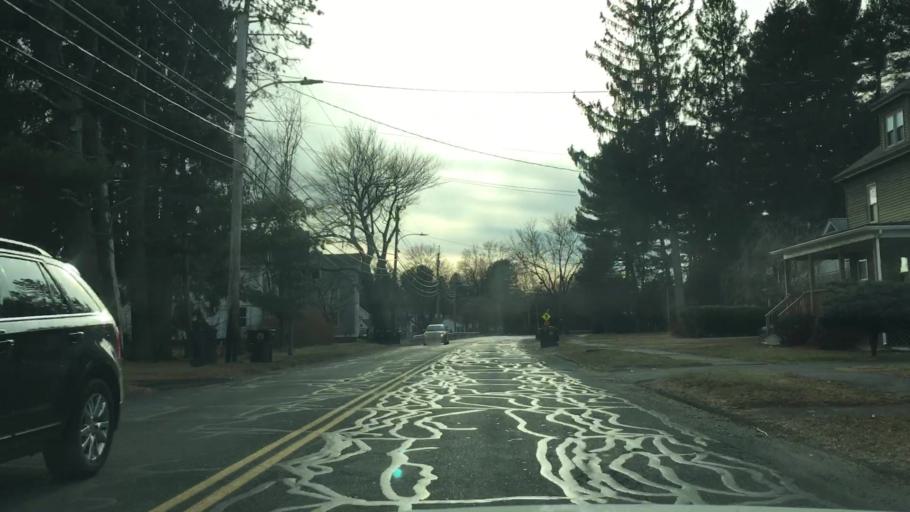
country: US
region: Massachusetts
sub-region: Hampden County
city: Westfield
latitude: 42.1138
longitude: -72.7537
